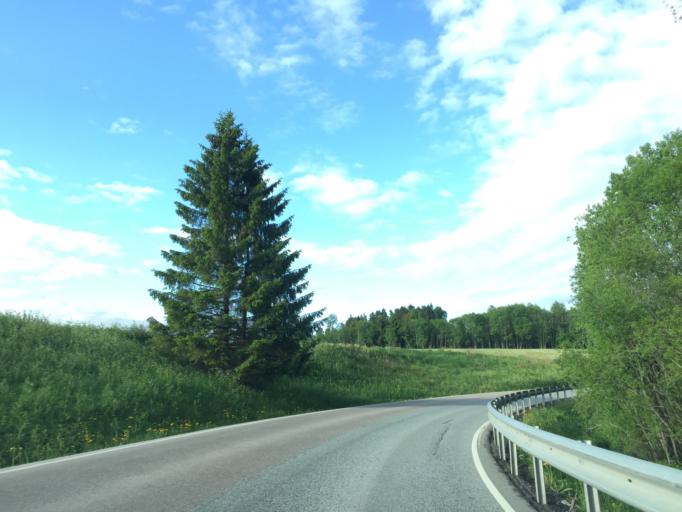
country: NO
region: Akershus
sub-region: Sorum
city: Sorumsand
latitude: 59.9914
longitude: 11.2961
